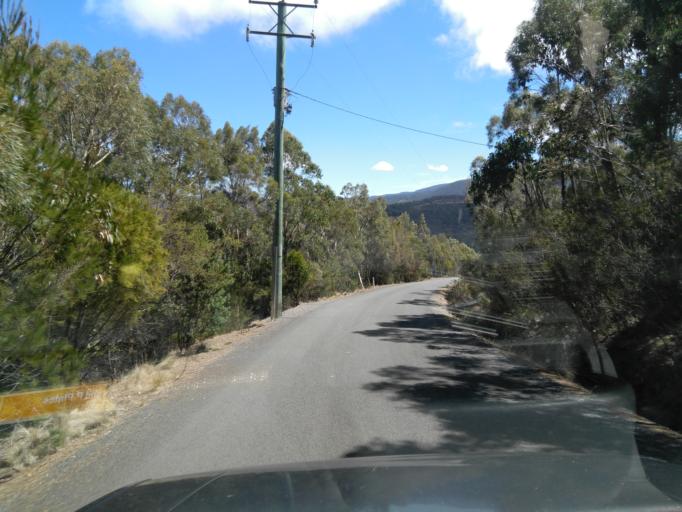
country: AU
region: Tasmania
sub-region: Kingborough
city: Taroona
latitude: -42.9507
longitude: 147.3211
